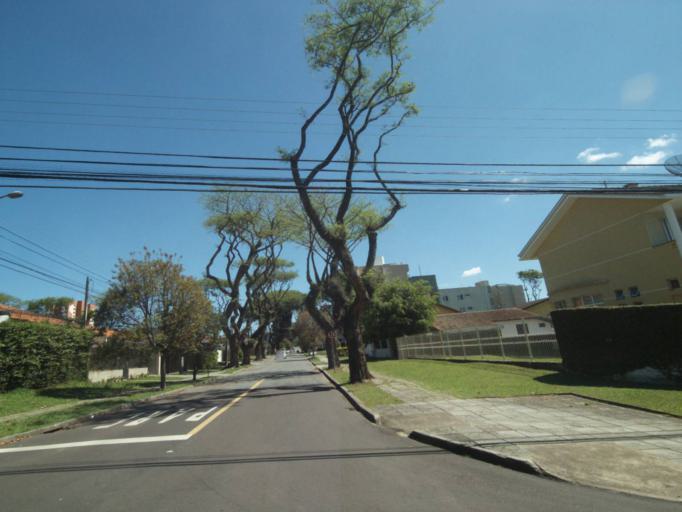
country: BR
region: Parana
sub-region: Curitiba
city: Curitiba
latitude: -25.3926
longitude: -49.2426
